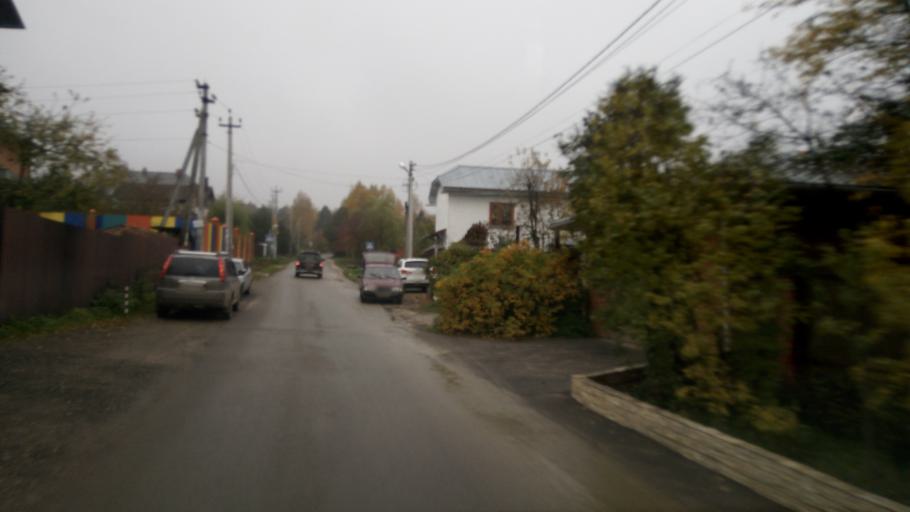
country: RU
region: Moskovskaya
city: Firsanovka
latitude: 55.9300
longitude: 37.2551
